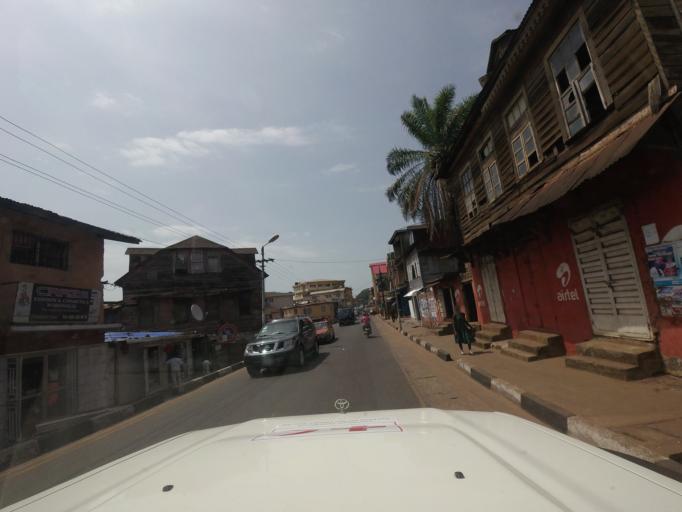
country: SL
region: Western Area
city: Freetown
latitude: 8.4819
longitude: -13.2360
